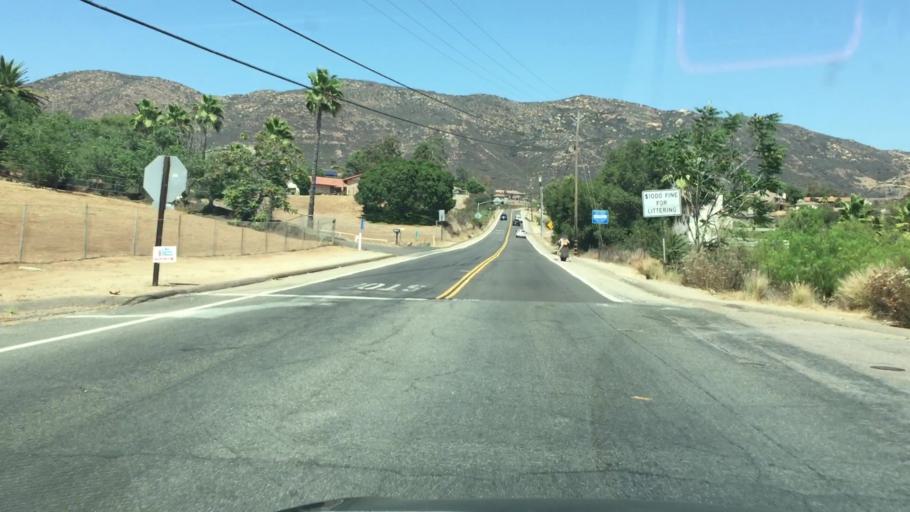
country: US
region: California
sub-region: San Diego County
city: Jamul
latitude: 32.7303
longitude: -116.8563
